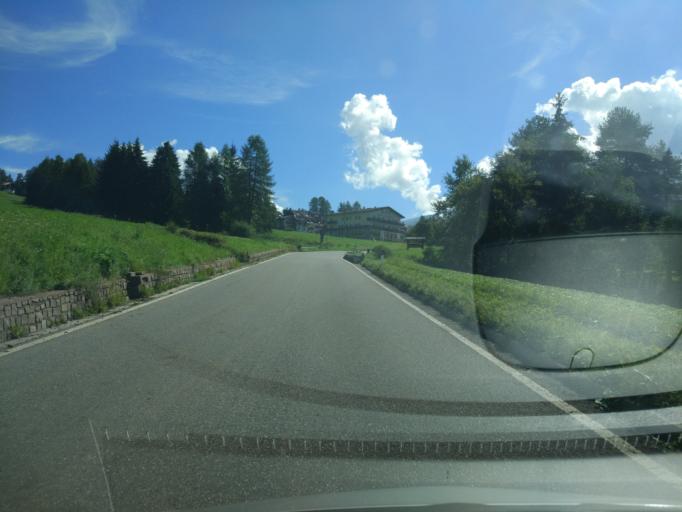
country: IT
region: Trentino-Alto Adige
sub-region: Provincia di Trento
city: Predazzo
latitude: 46.3151
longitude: 11.6573
